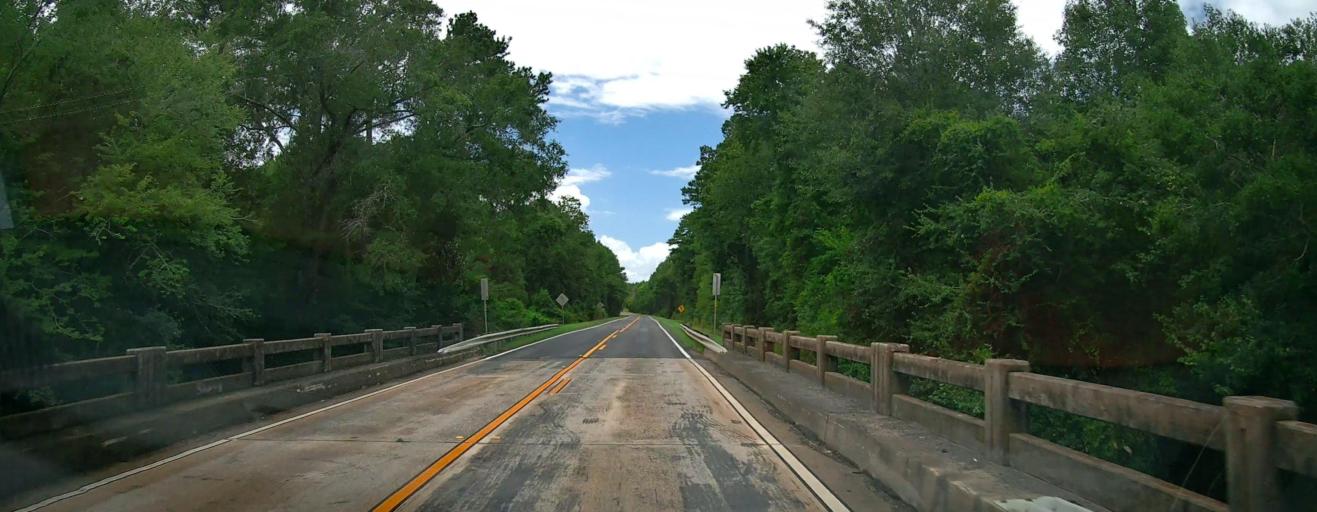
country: US
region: Georgia
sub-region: Wilcox County
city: Rochelle
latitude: 32.0886
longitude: -83.5955
